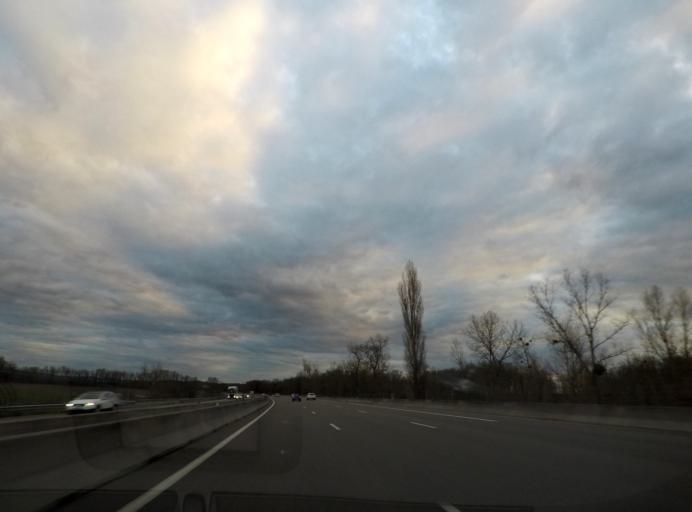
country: FR
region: Rhone-Alpes
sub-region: Departement de l'Ain
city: Saint-Martin-du-Mont
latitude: 46.0898
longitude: 5.2887
